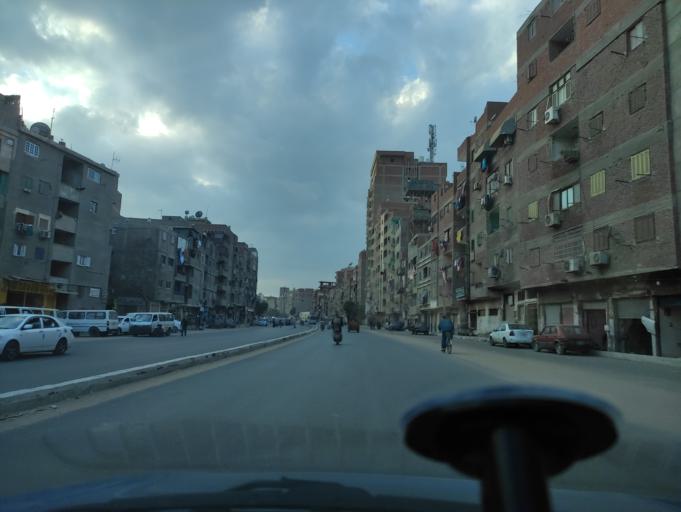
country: EG
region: Muhafazat al Qalyubiyah
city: Al Khankah
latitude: 30.1378
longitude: 31.3483
